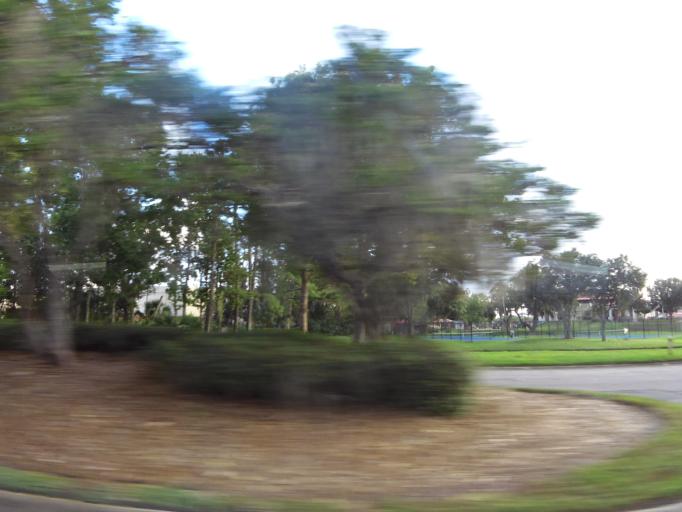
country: US
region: Florida
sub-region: Saint Johns County
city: Sawgrass
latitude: 30.1971
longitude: -81.3829
